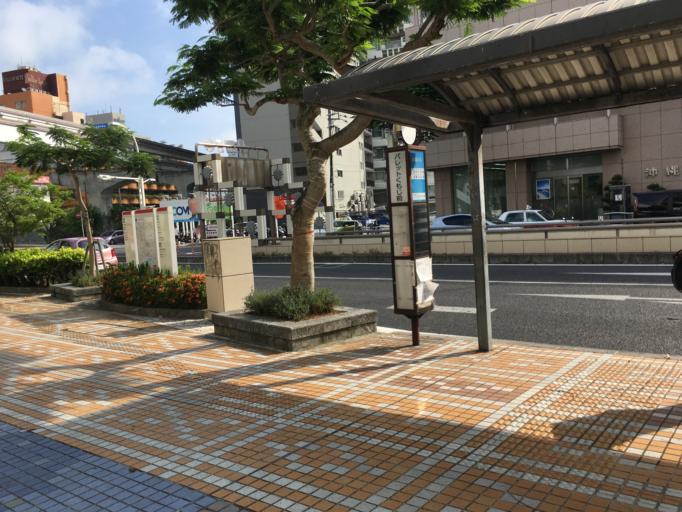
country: JP
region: Okinawa
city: Naha-shi
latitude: 26.2144
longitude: 127.6800
